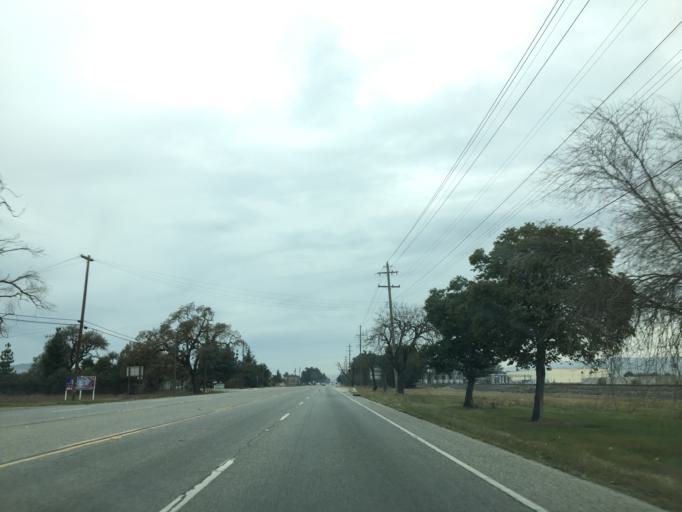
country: US
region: California
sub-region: Santa Clara County
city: San Martin
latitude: 37.0756
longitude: -121.6048
